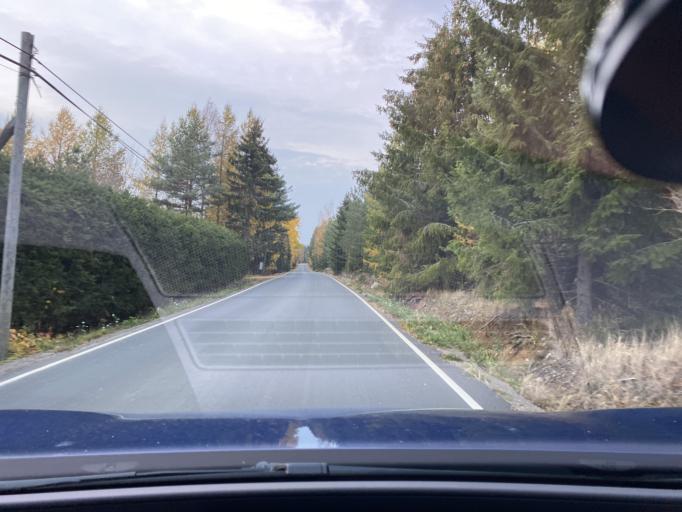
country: FI
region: Varsinais-Suomi
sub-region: Loimaa
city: Alastaro
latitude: 61.0910
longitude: 22.9088
